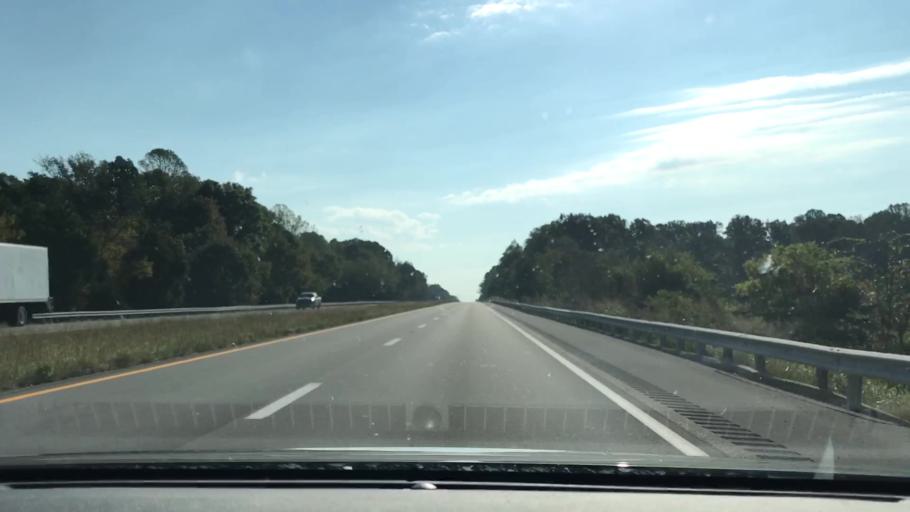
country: US
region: Kentucky
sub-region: Adair County
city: Columbia
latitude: 37.0791
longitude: -85.2405
